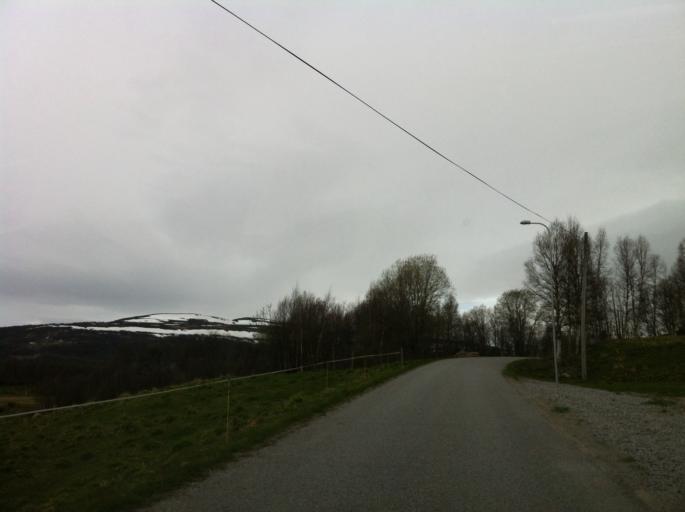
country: NO
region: Sor-Trondelag
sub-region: Tydal
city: Aas
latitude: 62.6350
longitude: 12.4450
